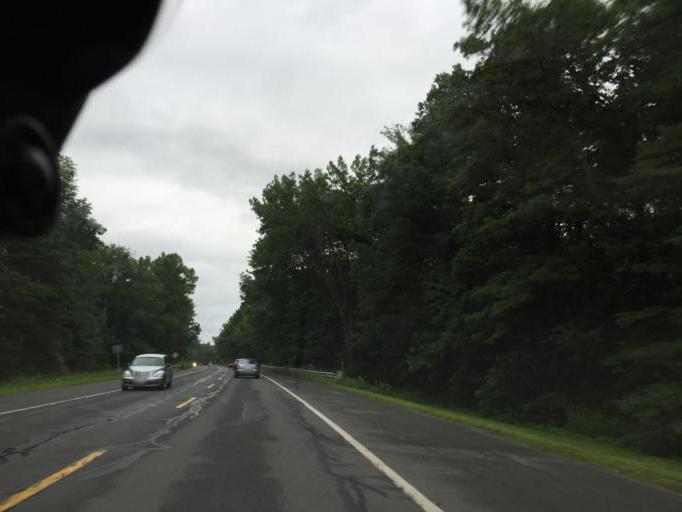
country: US
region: Massachusetts
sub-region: Berkshire County
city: Sheffield
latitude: 42.0842
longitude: -73.3403
